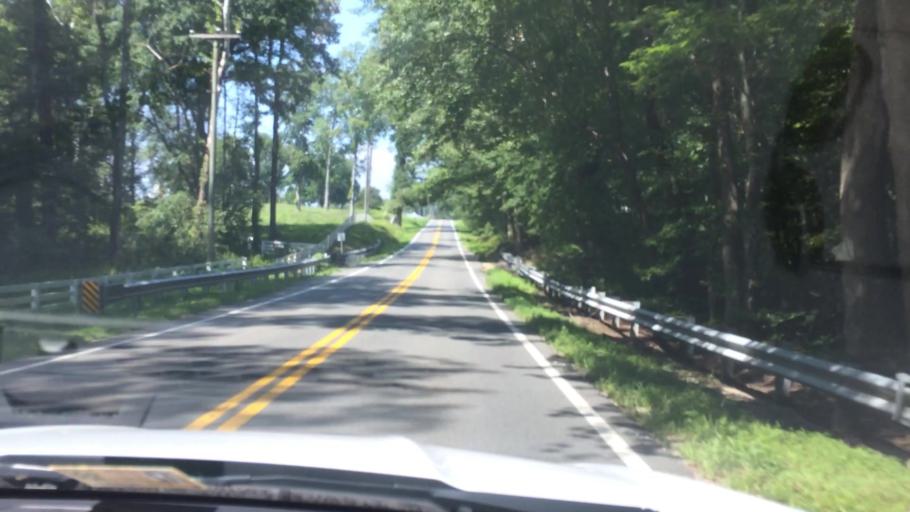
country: US
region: Virginia
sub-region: New Kent County
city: New Kent
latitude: 37.5242
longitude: -77.0515
